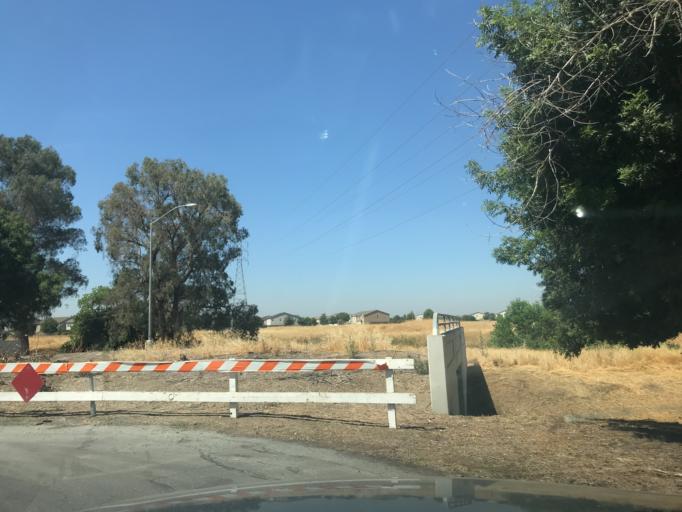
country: US
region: California
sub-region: Merced County
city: Merced
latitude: 37.3401
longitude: -120.4852
